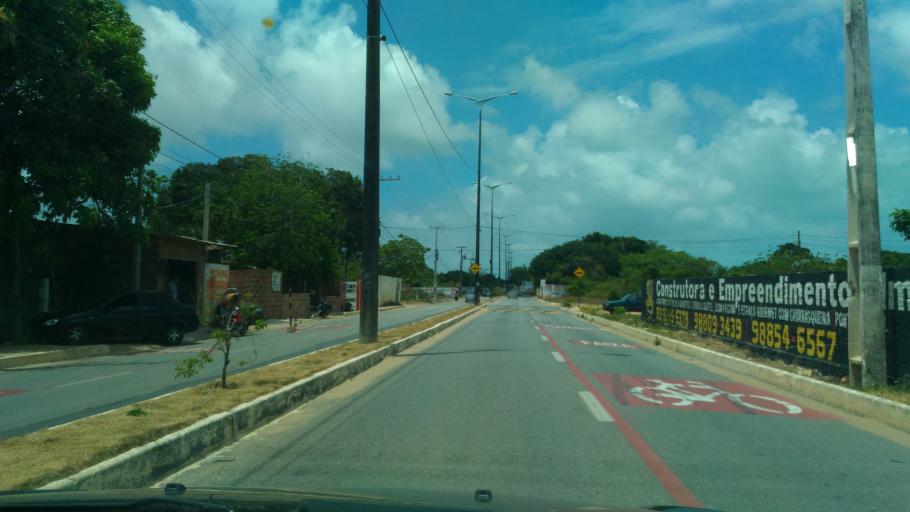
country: BR
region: Paraiba
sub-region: Joao Pessoa
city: Joao Pessoa
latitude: -7.1491
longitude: -34.8169
